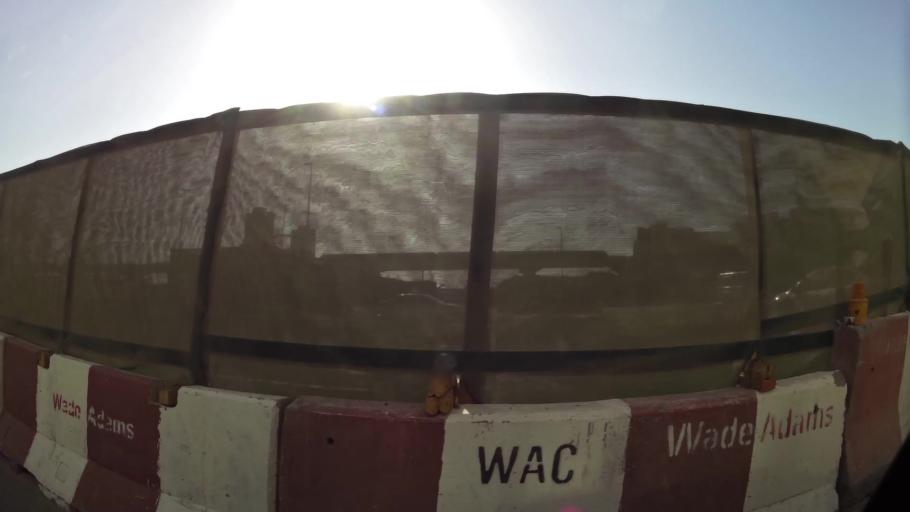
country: AE
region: Ash Shariqah
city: Sharjah
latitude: 25.2395
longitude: 55.2968
